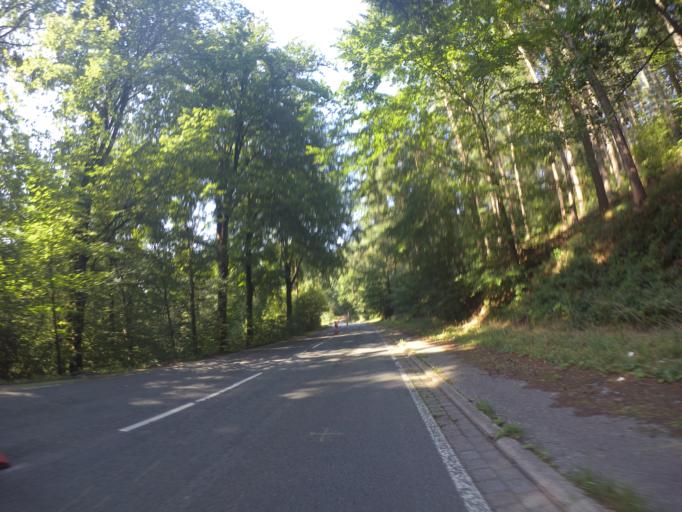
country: DE
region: North Rhine-Westphalia
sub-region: Regierungsbezirk Arnsberg
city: Schwelm
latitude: 51.2556
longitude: 7.2912
